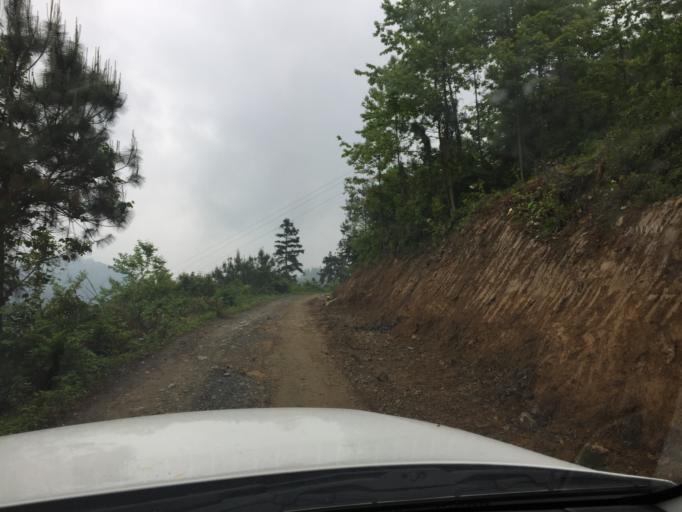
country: CN
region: Guizhou Sheng
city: Donghua
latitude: 28.0656
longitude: 108.0877
